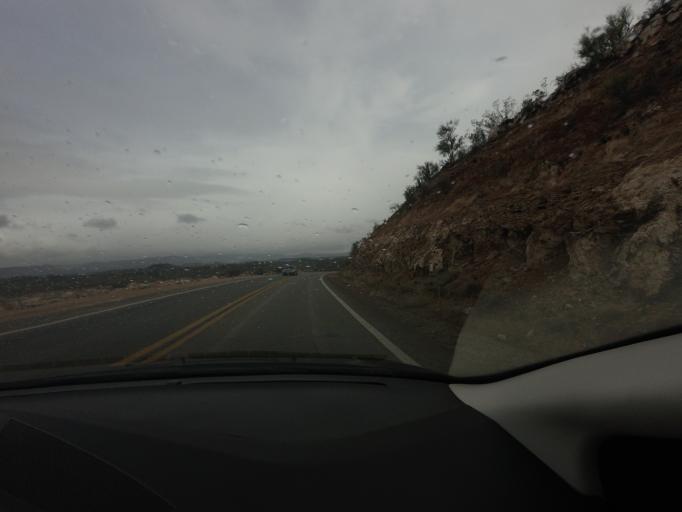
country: US
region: Arizona
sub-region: Yavapai County
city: Lake Montezuma
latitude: 34.6451
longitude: -111.8175
